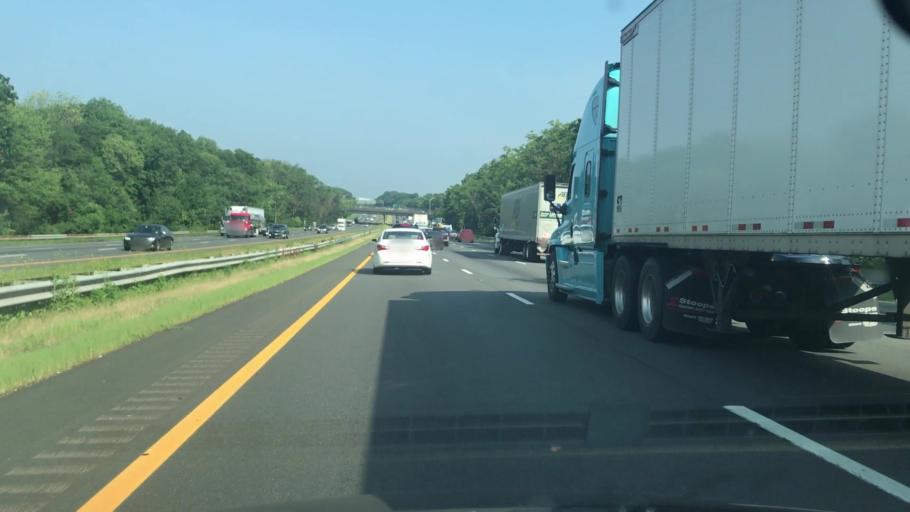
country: US
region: New Jersey
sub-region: Middlesex County
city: Metuchen
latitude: 40.5389
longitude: -74.3854
